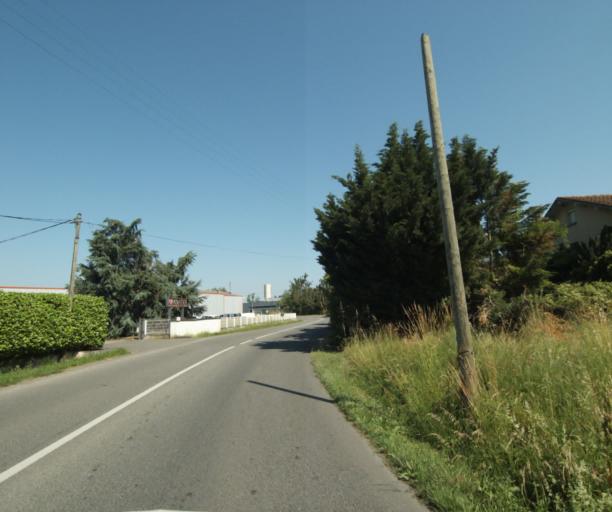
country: FR
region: Midi-Pyrenees
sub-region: Departement du Tarn-et-Garonne
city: Montbeton
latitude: 44.0190
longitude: 1.3239
